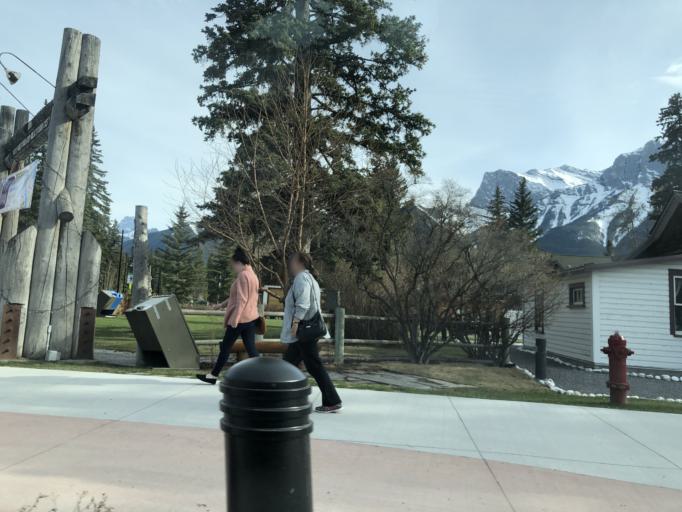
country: CA
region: Alberta
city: Canmore
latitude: 51.0893
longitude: -115.3563
